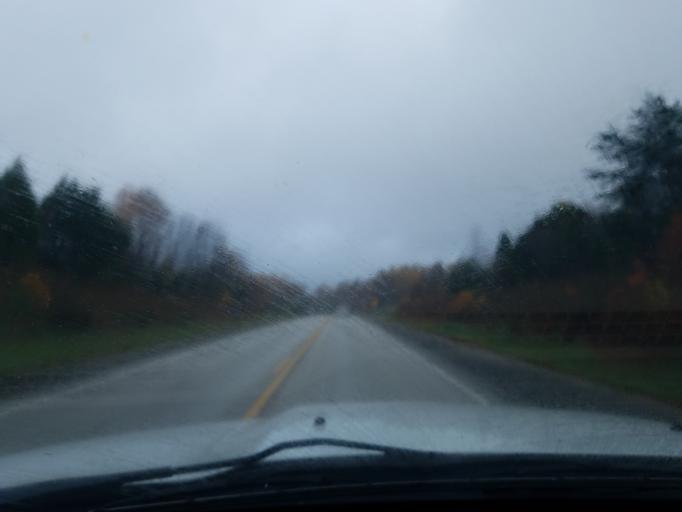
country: US
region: Kentucky
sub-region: Larue County
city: Hodgenville
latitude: 37.4715
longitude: -85.6052
